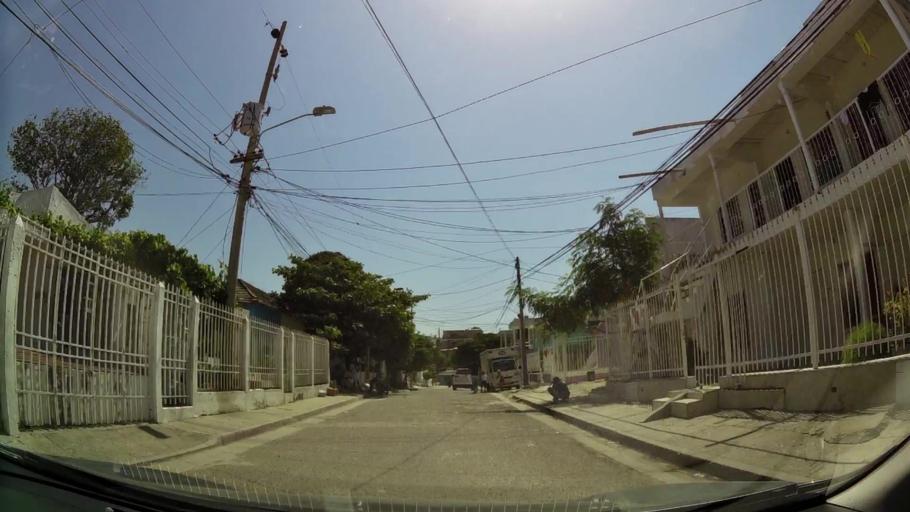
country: CO
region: Bolivar
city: Cartagena
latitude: 10.4368
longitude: -75.5237
